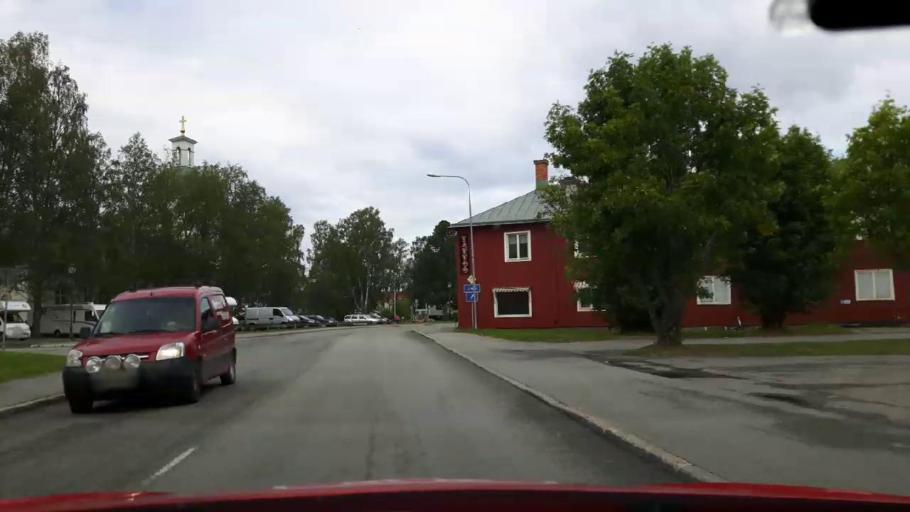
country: SE
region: Jaemtland
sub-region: Stroemsunds Kommun
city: Stroemsund
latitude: 63.8508
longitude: 15.5573
